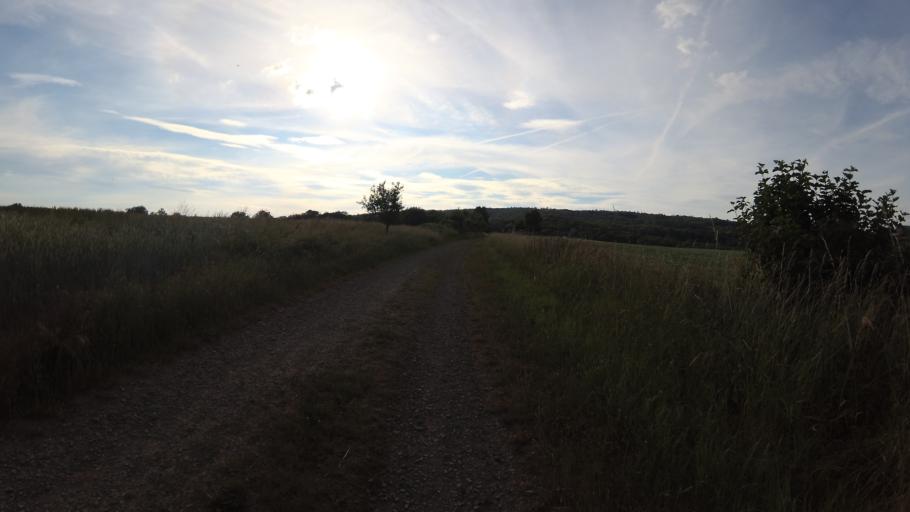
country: DE
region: Rheinland-Pfalz
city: Frohnhofen
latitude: 49.4584
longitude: 7.3129
